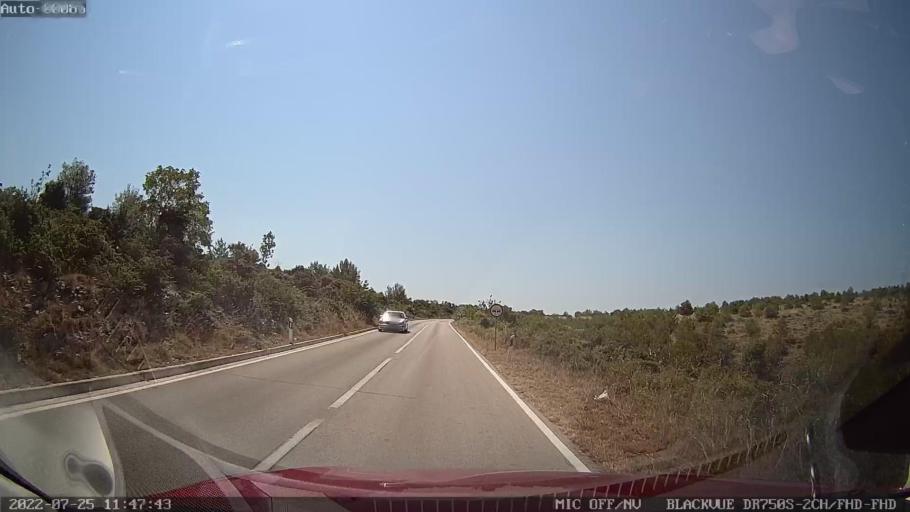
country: HR
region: Zadarska
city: Razanac
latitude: 44.2359
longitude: 15.3024
